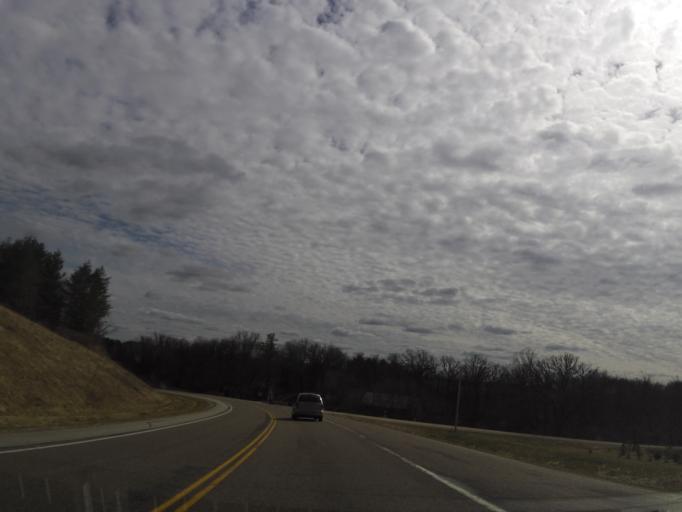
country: US
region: Minnesota
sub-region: Olmsted County
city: Stewartville
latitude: 43.8960
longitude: -92.4114
